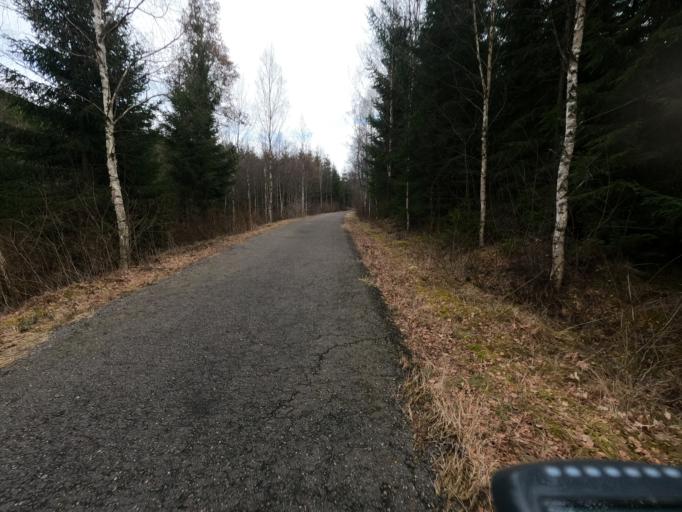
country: SE
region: Joenkoeping
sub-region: Varnamo Kommun
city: Rydaholm
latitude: 56.8389
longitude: 14.2389
